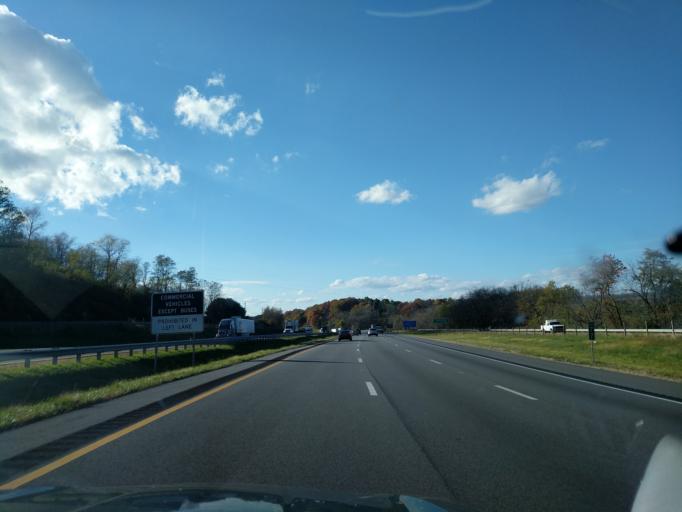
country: US
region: Virginia
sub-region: Wythe County
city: Wytheville
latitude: 36.9389
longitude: -81.0027
